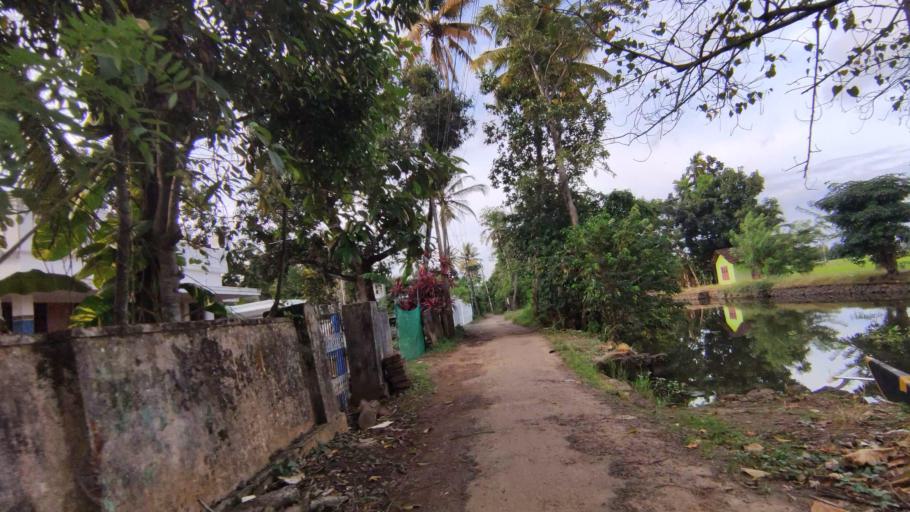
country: IN
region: Kerala
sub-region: Kottayam
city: Kottayam
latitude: 9.5994
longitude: 76.4398
